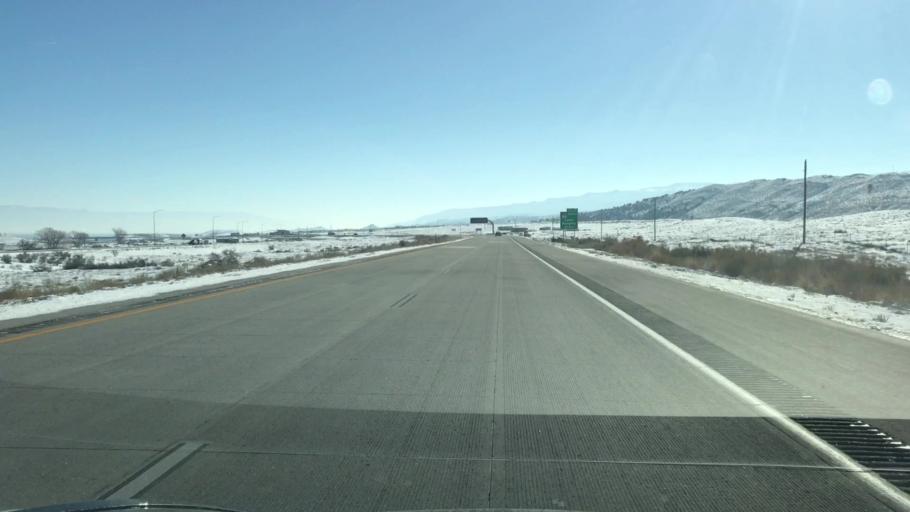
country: US
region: Colorado
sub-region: Mesa County
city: Loma
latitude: 39.1829
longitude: -108.8301
